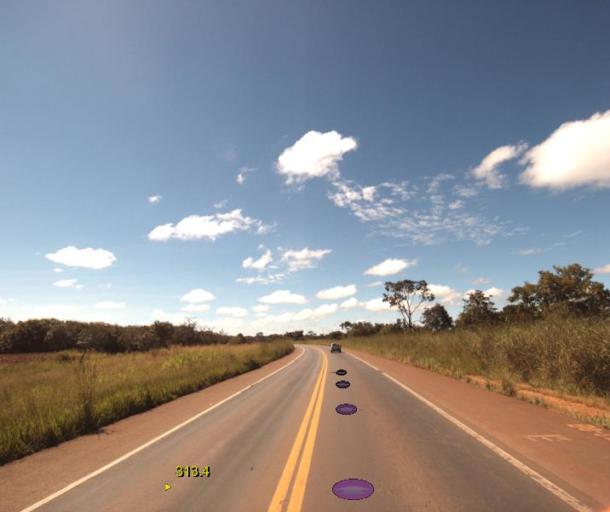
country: BR
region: Goias
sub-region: Rialma
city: Rialma
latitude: -15.3947
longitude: -49.5463
